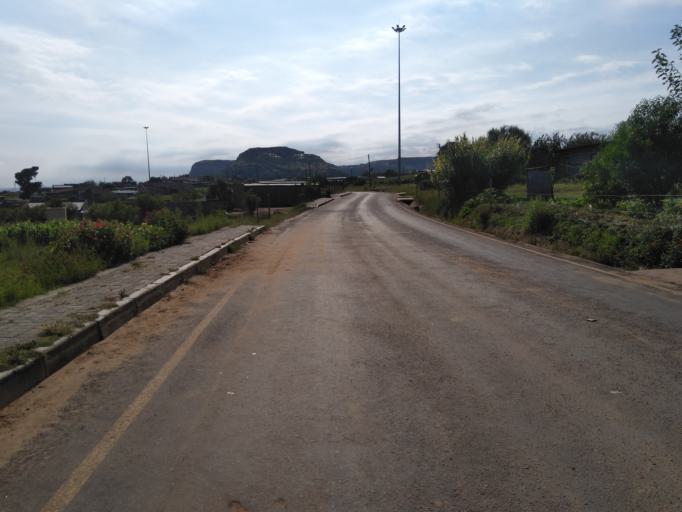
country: LS
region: Butha-Buthe
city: Butha-Buthe
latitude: -28.7743
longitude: 28.2476
